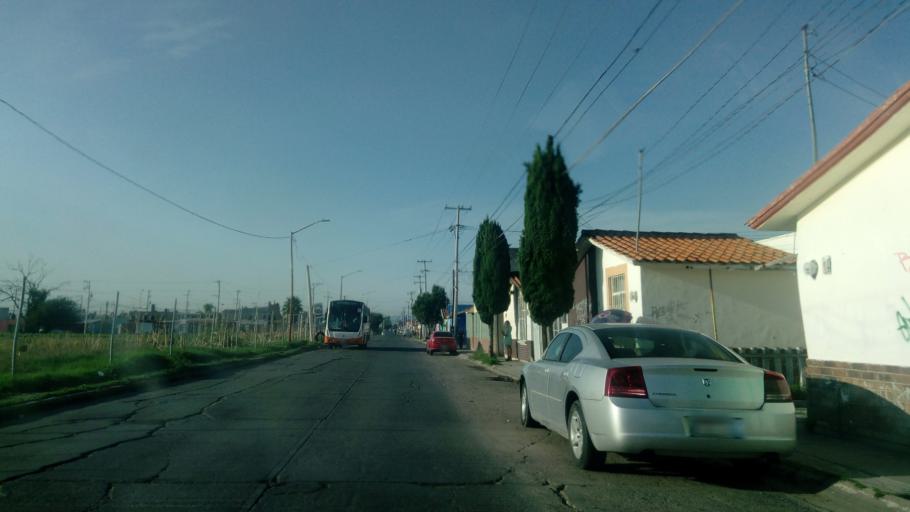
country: MX
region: Durango
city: Victoria de Durango
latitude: 24.0659
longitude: -104.5861
